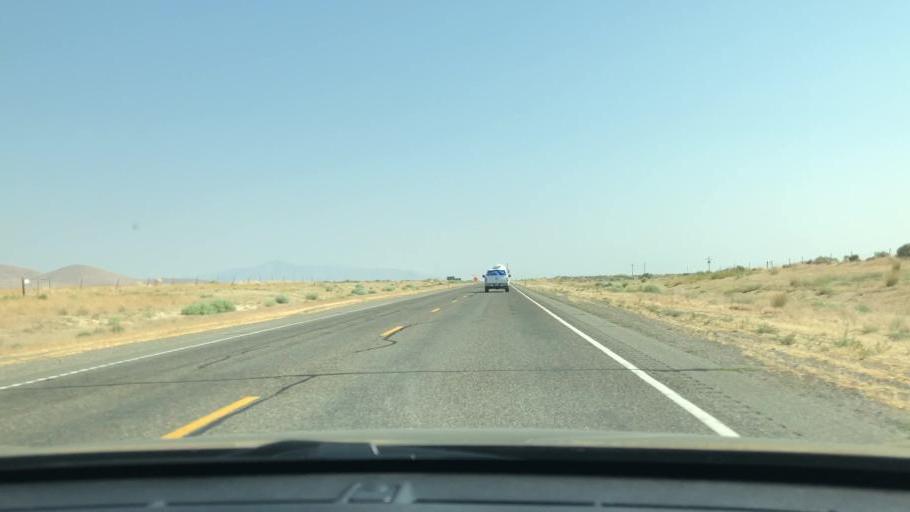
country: US
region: Nevada
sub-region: Humboldt County
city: Winnemucca
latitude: 41.1446
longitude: -117.6888
